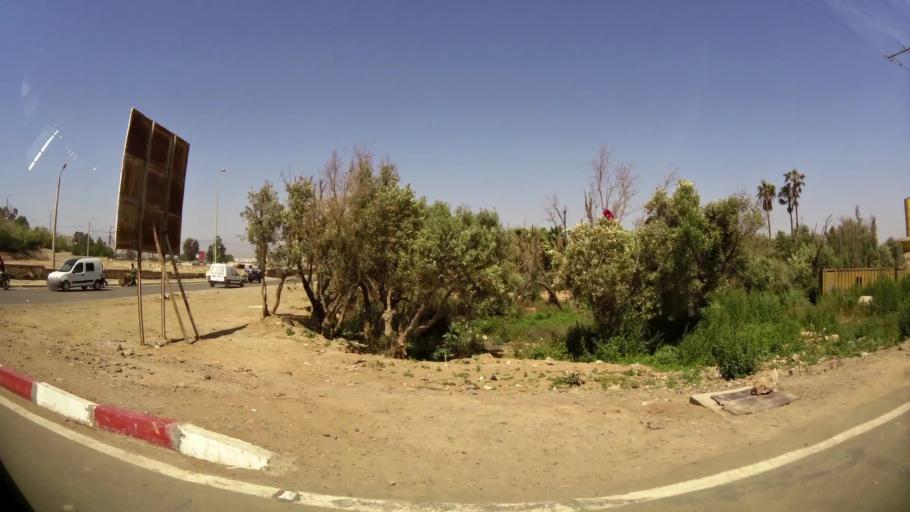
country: MA
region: Souss-Massa-Draa
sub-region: Inezgane-Ait Mellou
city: Inezgane
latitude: 30.3521
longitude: -9.5314
